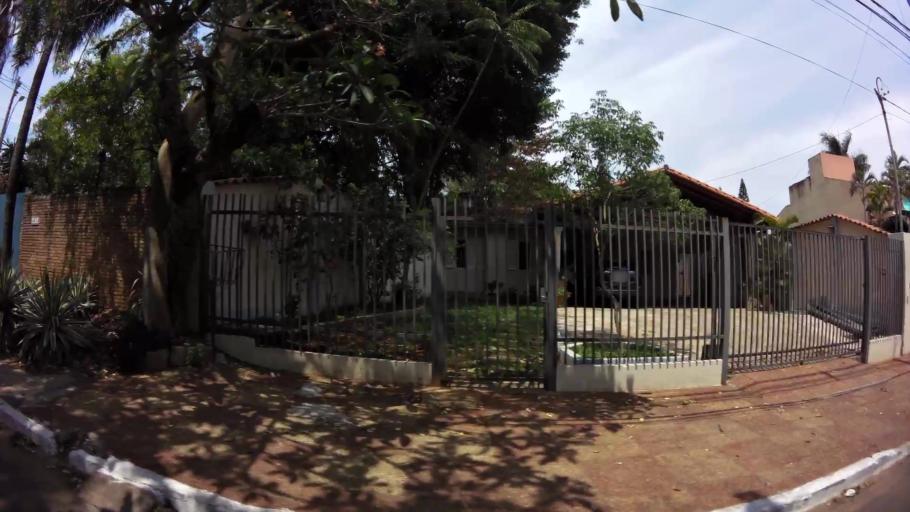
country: PY
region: Central
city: Lambare
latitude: -25.2998
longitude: -57.5694
